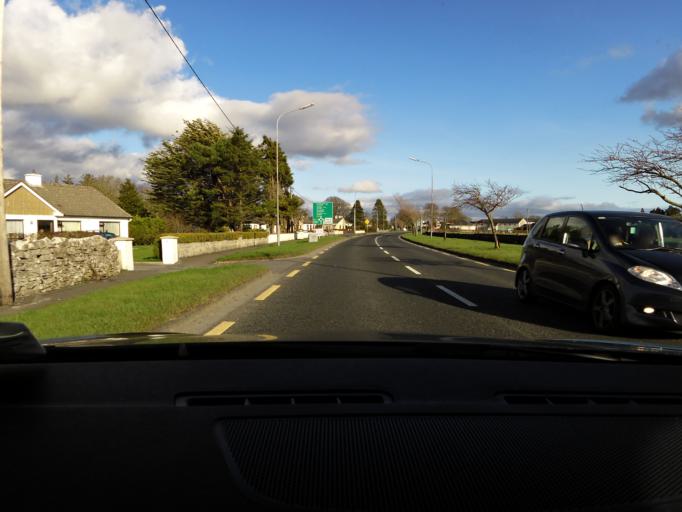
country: IE
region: Connaught
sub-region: Roscommon
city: Roscommon
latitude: 53.6387
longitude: -8.1949
